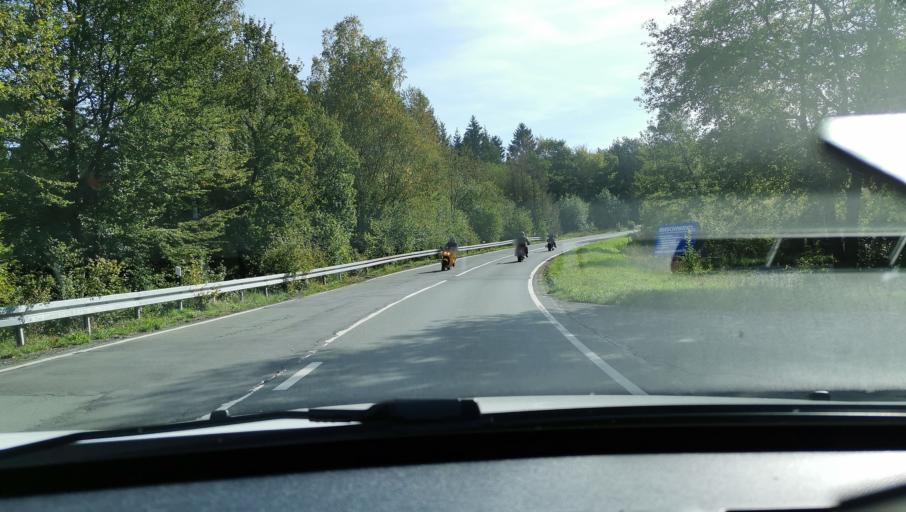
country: DE
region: North Rhine-Westphalia
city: Kierspe
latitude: 51.1200
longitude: 7.6147
